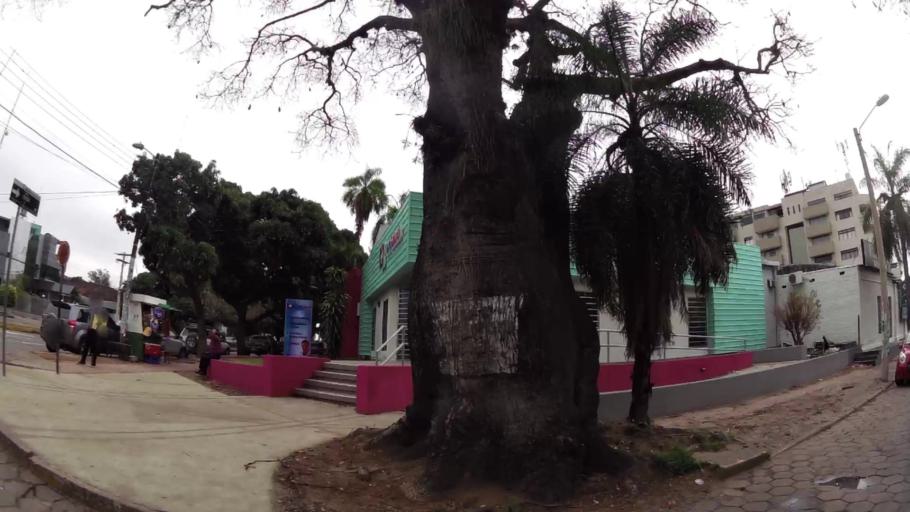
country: BO
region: Santa Cruz
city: Santa Cruz de la Sierra
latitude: -17.7744
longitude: -63.1834
